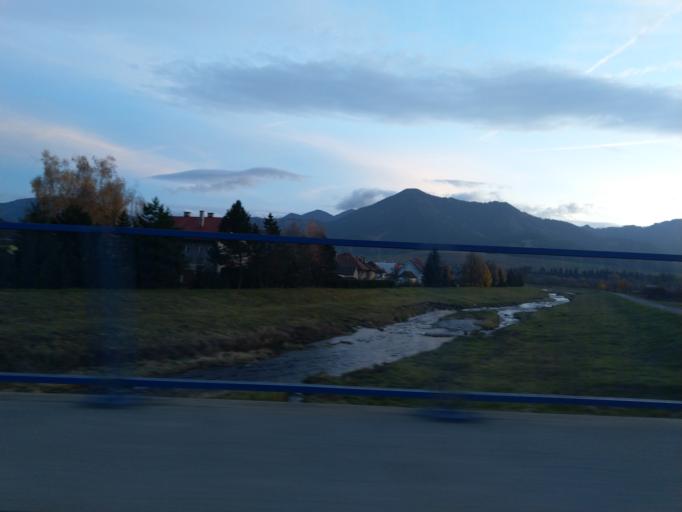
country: SK
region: Zilinsky
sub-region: Okres Liptovsky Mikulas
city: Liptovsky Mikulas
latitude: 49.0764
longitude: 19.6456
